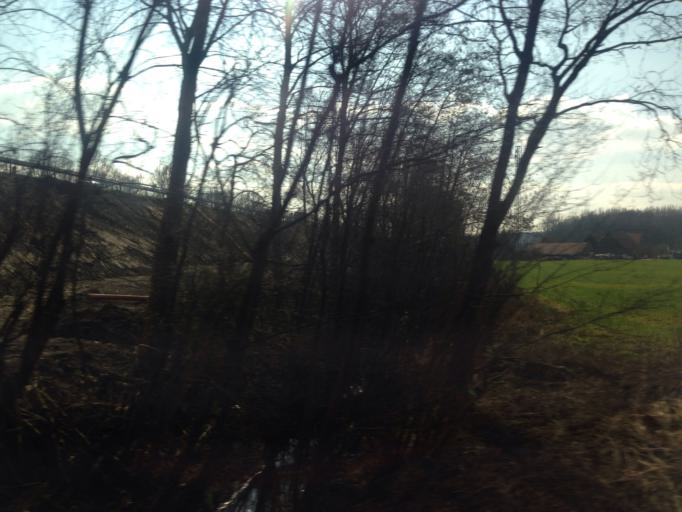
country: DE
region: North Rhine-Westphalia
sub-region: Regierungsbezirk Munster
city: Muenster
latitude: 52.0153
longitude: 7.5862
